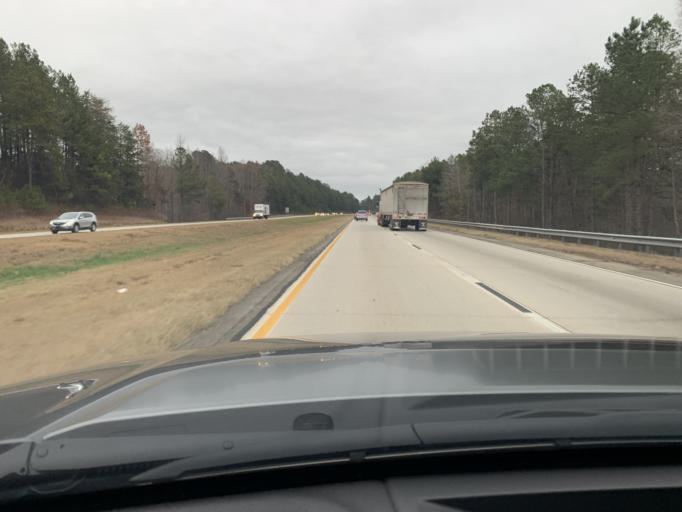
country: US
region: Georgia
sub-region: Hall County
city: Lula
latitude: 34.3612
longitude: -83.7448
